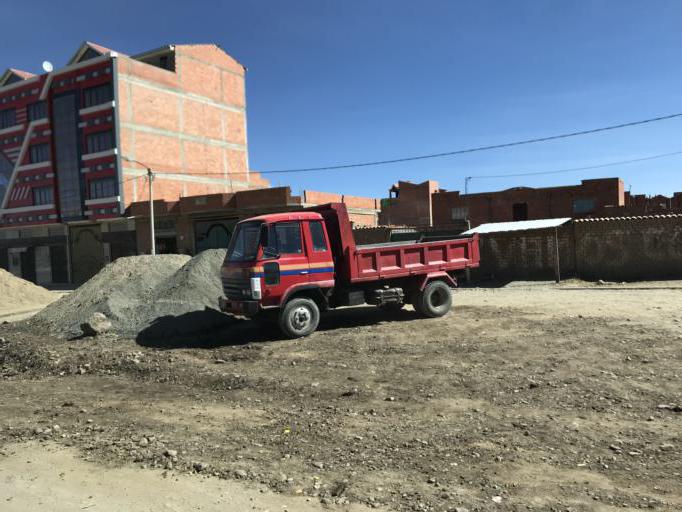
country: BO
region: La Paz
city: La Paz
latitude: -16.5024
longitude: -68.2437
